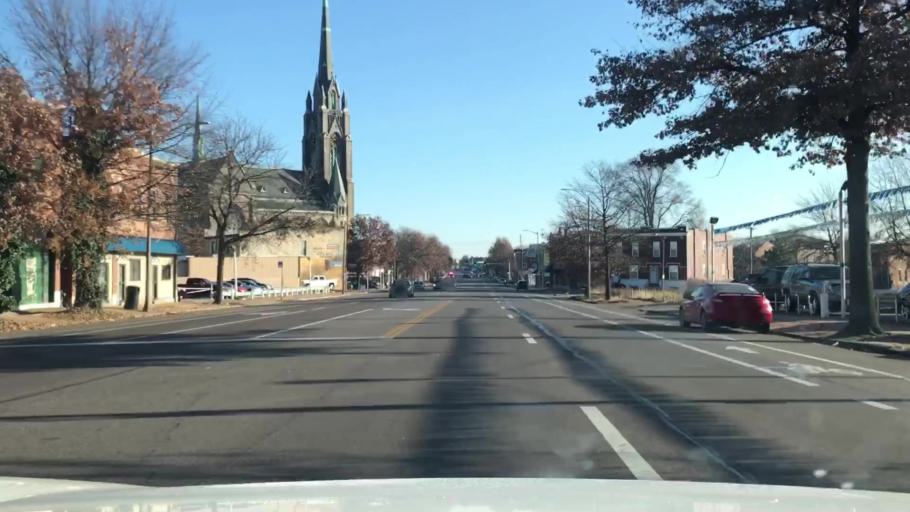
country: US
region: Missouri
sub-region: City of Saint Louis
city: St. Louis
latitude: 38.6027
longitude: -90.2280
